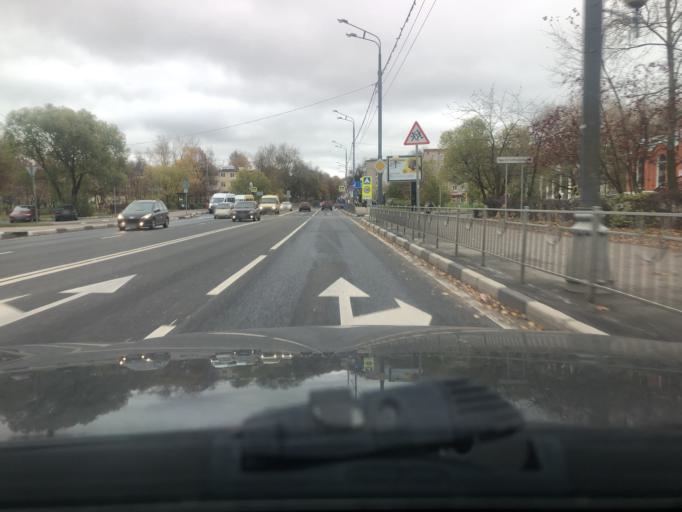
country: RU
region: Moskovskaya
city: Sergiyev Posad
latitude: 56.3221
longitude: 38.1365
